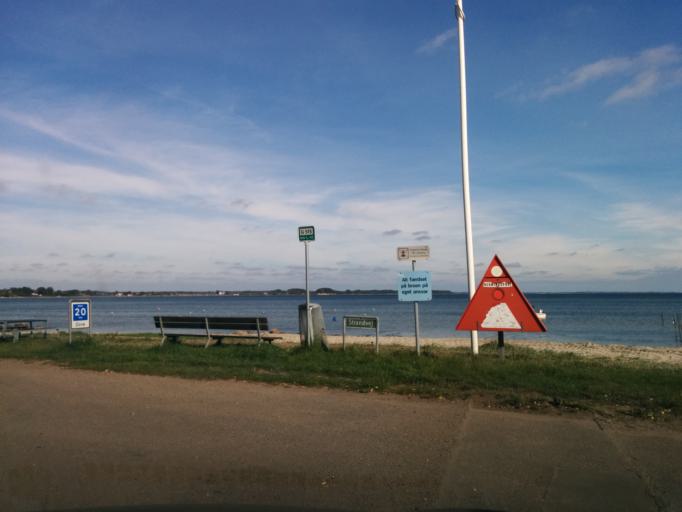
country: DK
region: South Denmark
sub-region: Kolding Kommune
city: Sonder Bjert
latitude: 55.4120
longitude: 9.5957
